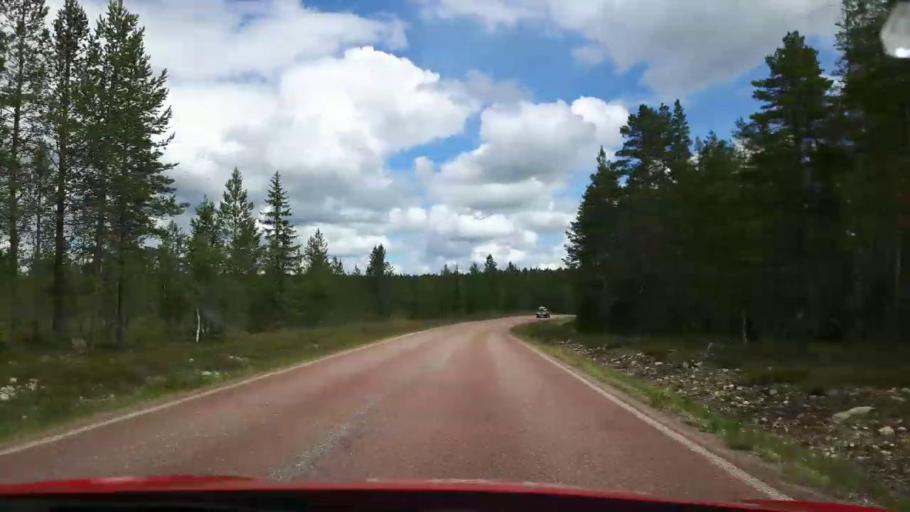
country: NO
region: Hedmark
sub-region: Trysil
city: Innbygda
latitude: 61.9082
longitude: 13.0002
